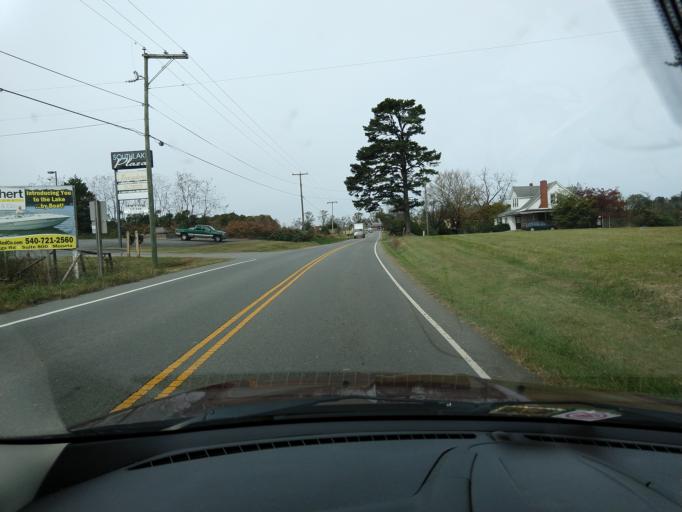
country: US
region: Virginia
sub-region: Franklin County
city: Union Hall
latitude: 36.9944
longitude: -79.6864
